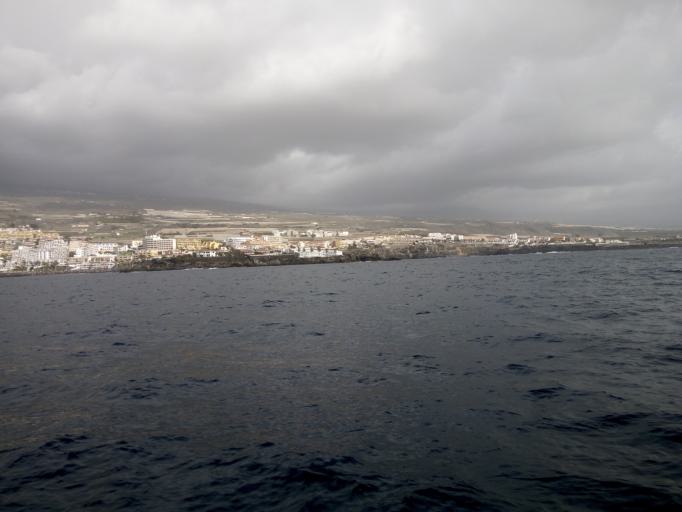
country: ES
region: Canary Islands
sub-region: Provincia de Santa Cruz de Tenerife
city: Guia de Isora
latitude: 28.2280
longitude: -16.8486
